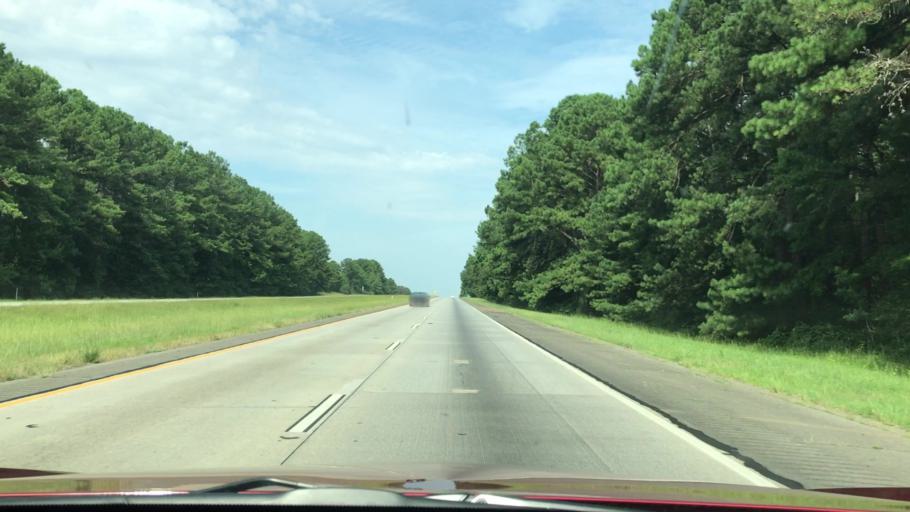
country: US
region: Georgia
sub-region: Taliaferro County
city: Crawfordville
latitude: 33.4999
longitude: -82.7968
